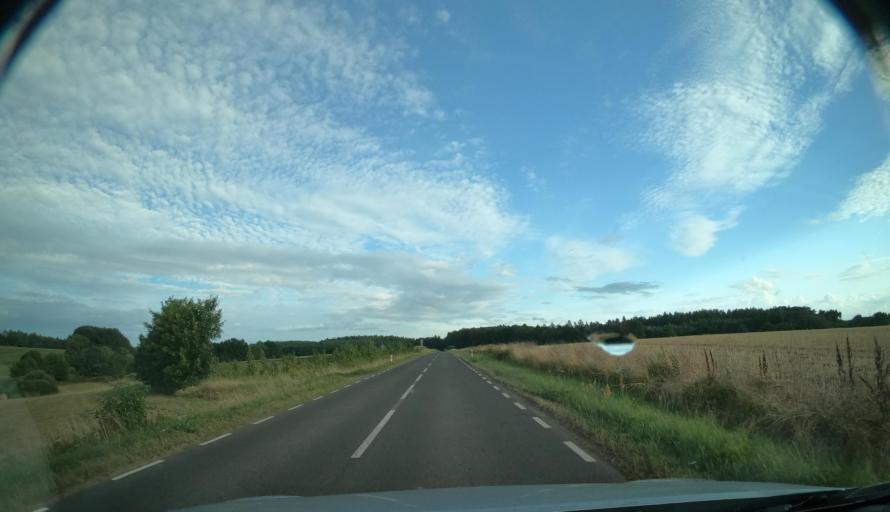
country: PL
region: West Pomeranian Voivodeship
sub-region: Powiat kamienski
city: Golczewo
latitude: 53.8438
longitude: 14.9535
